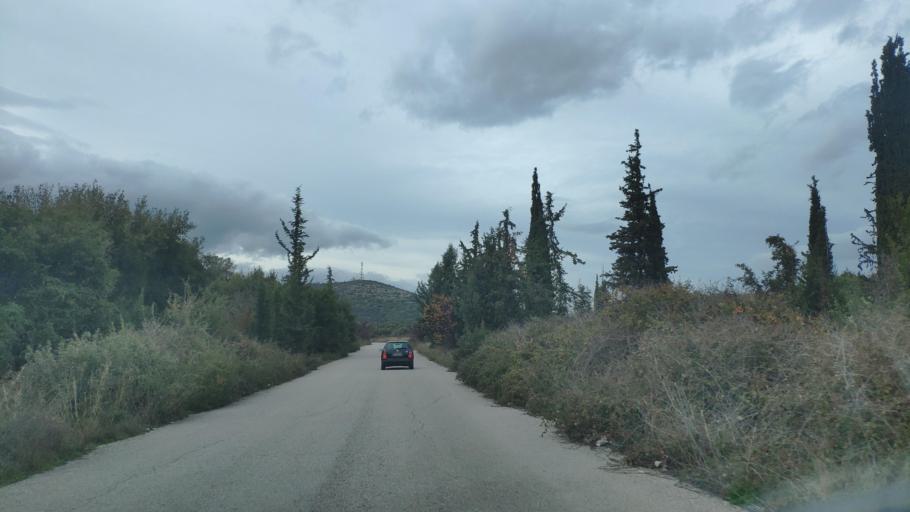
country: GR
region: Peloponnese
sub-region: Nomos Korinthias
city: Ayios Vasilios
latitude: 37.7928
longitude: 22.7315
